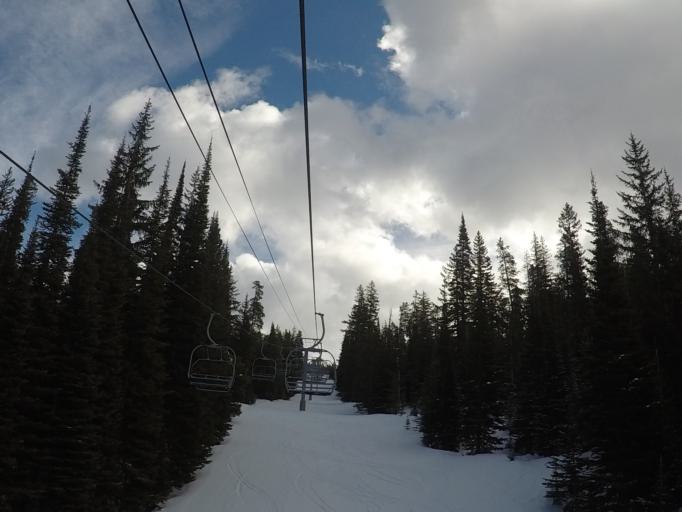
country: US
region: Montana
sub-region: Granite County
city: Philipsburg
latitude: 46.2524
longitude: -113.2245
